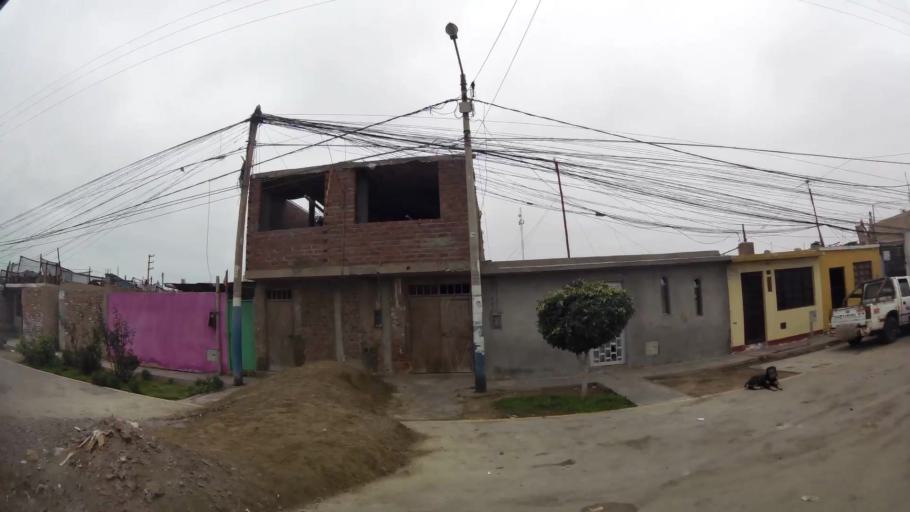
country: PE
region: Ica
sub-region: Provincia de Pisco
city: Pisco
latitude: -13.7334
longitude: -76.2189
